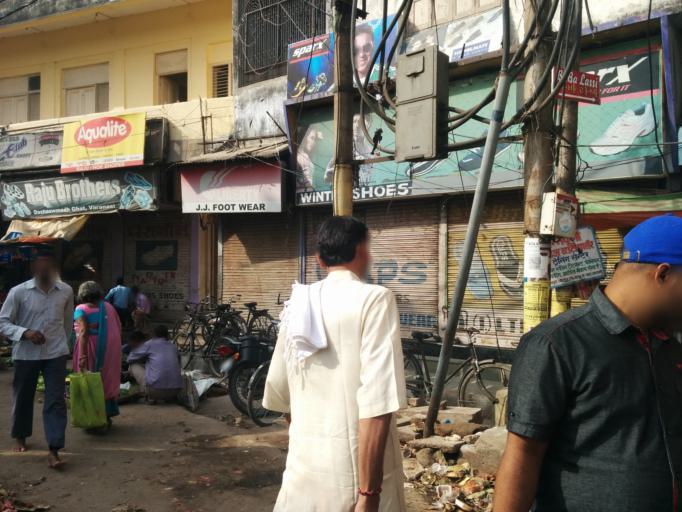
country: IN
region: Uttar Pradesh
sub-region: Varanasi
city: Varanasi
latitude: 25.3069
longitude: 83.0095
